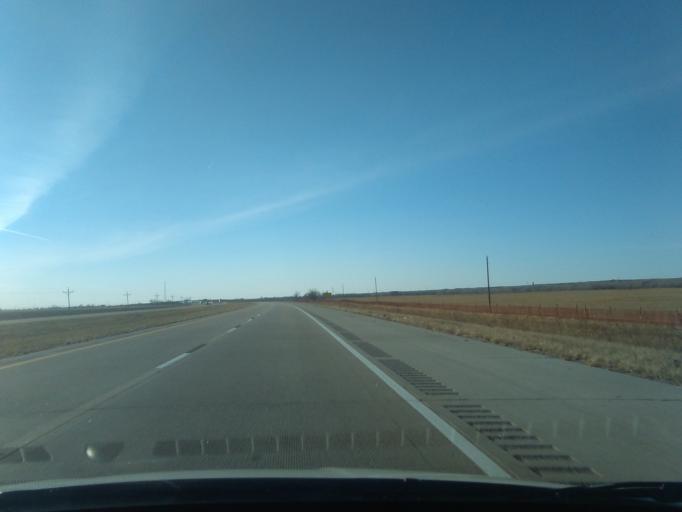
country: US
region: Colorado
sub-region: Sedgwick County
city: Julesburg
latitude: 41.0623
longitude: -102.0204
